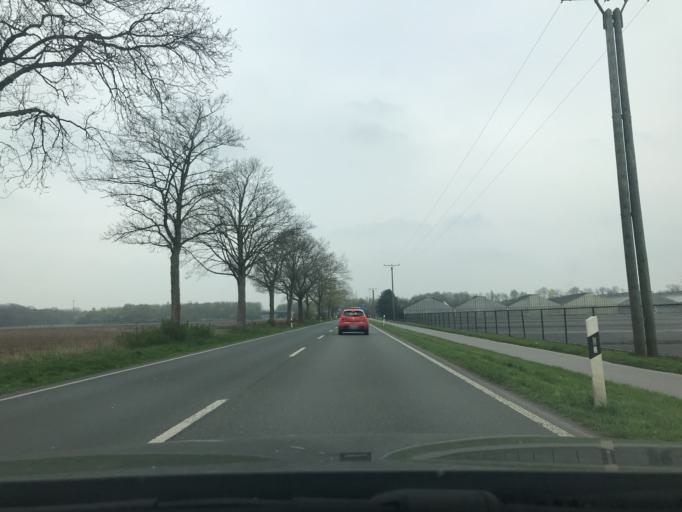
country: DE
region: North Rhine-Westphalia
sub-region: Regierungsbezirk Dusseldorf
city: Weeze
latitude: 51.6509
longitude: 6.1848
